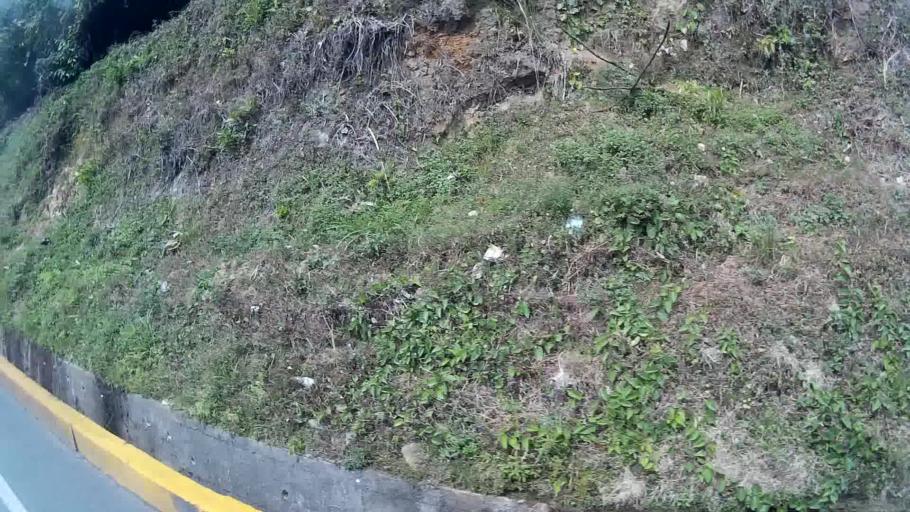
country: CO
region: Risaralda
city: Pereira
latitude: 4.8124
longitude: -75.7540
